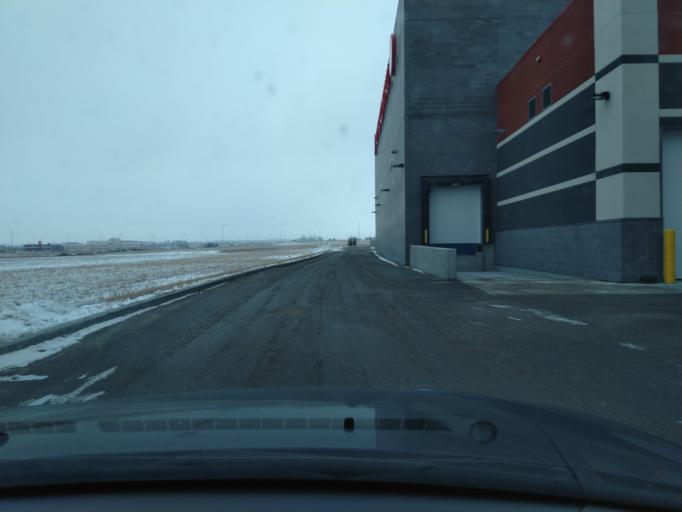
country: CA
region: Alberta
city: Airdrie
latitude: 51.1966
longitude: -113.9969
